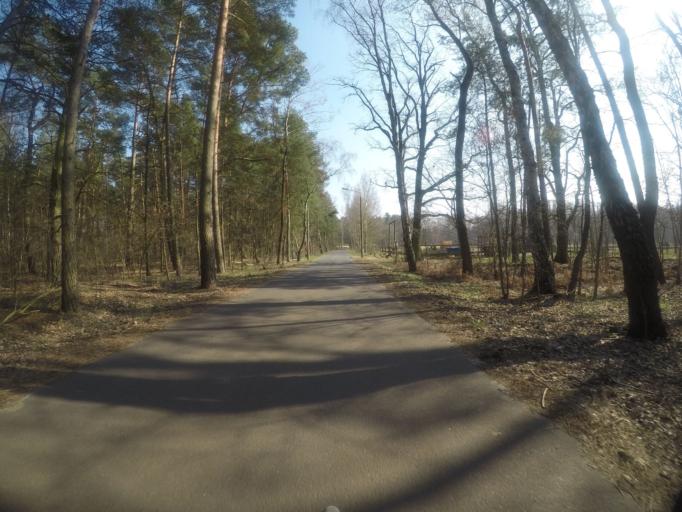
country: DE
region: Brandenburg
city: Bestensee
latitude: 52.2951
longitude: 13.7479
